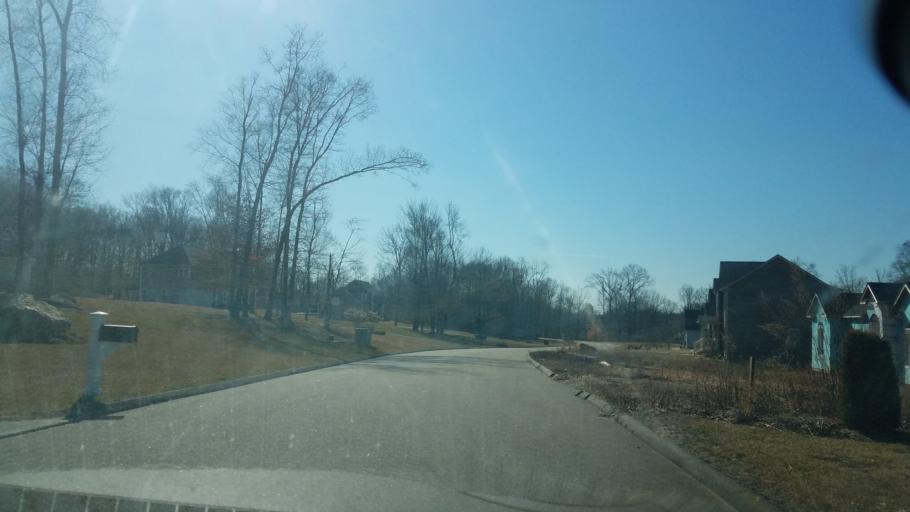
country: US
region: Connecticut
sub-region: Middlesex County
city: East Hampton
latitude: 41.5899
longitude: -72.4737
